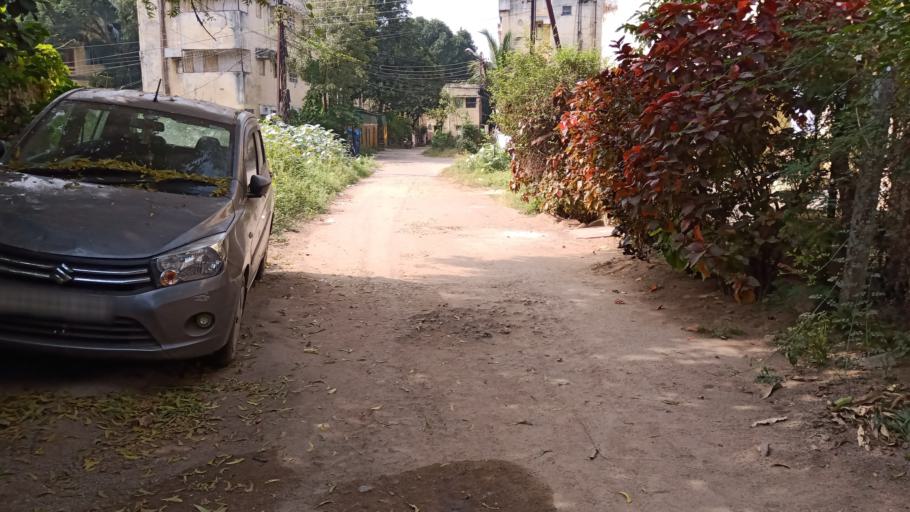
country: IN
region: Telangana
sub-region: Rangareddi
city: Kukatpalli
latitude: 17.4451
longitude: 78.4438
